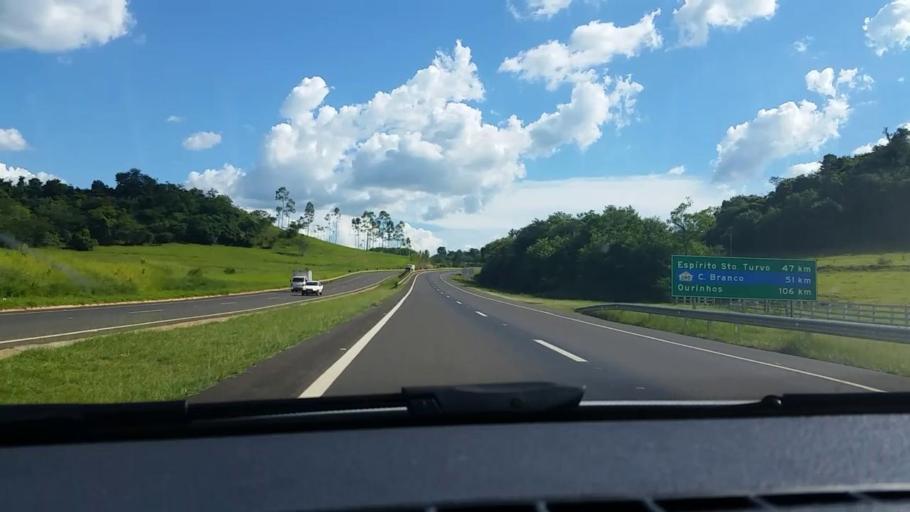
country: BR
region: Sao Paulo
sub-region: Bauru
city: Bauru
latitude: -22.4314
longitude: -49.1327
